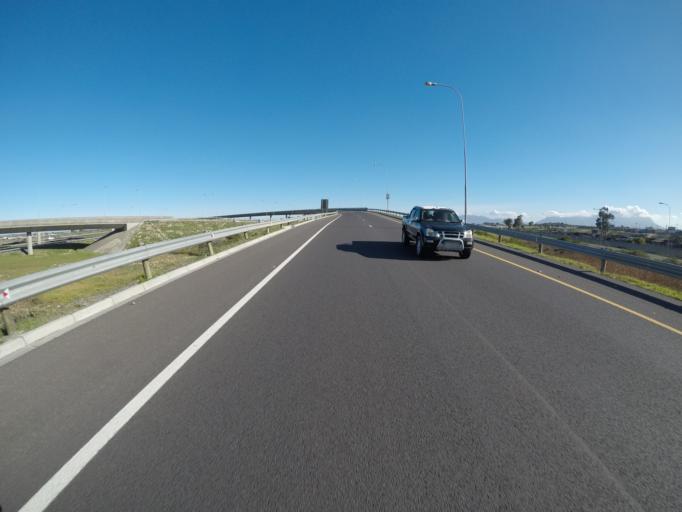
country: ZA
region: Western Cape
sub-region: City of Cape Town
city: Lansdowne
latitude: -33.9984
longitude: 18.6346
